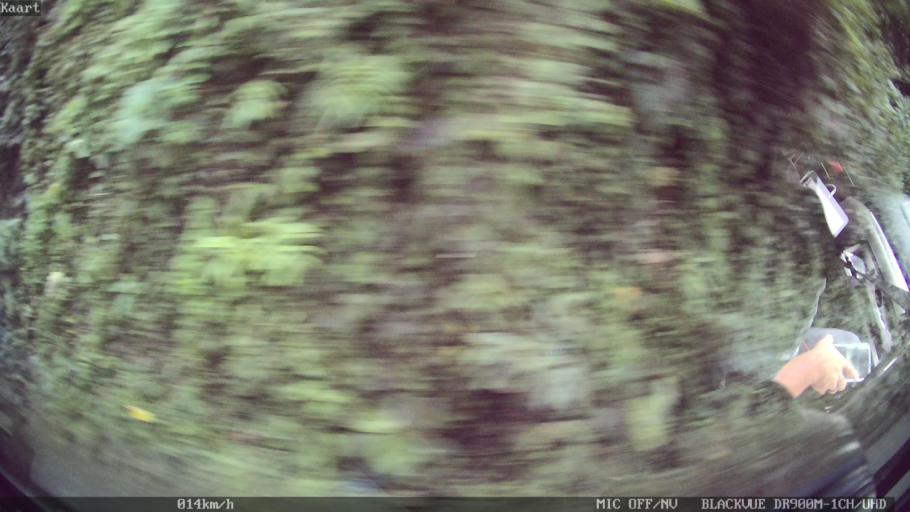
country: ID
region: Bali
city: Banjar Parekan
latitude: -8.5831
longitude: 115.2133
